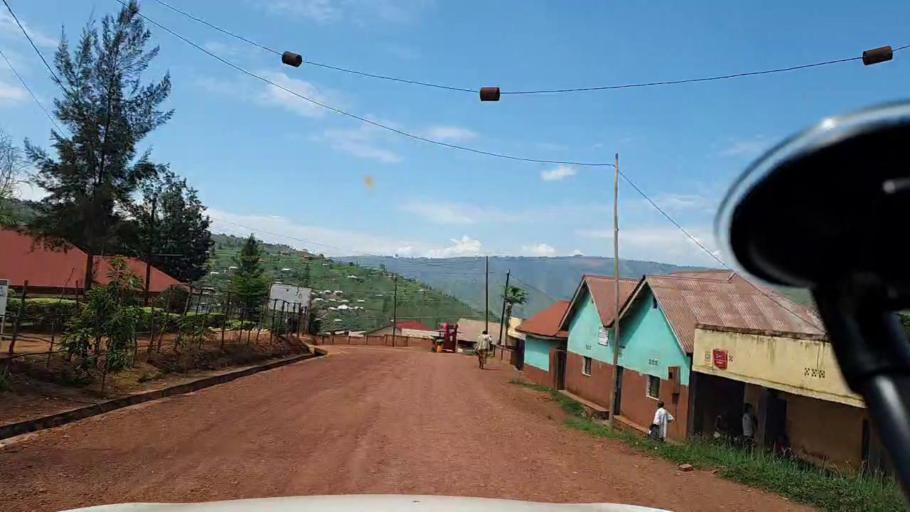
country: RW
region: Kigali
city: Kigali
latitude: -1.7998
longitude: 29.8954
